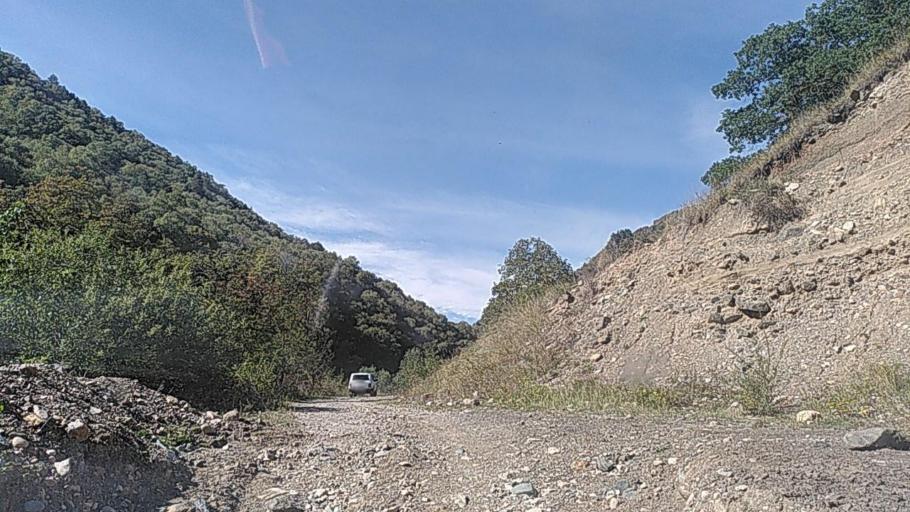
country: RU
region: Kabardino-Balkariya
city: Kamennomostskoye
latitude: 43.7229
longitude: 42.8536
